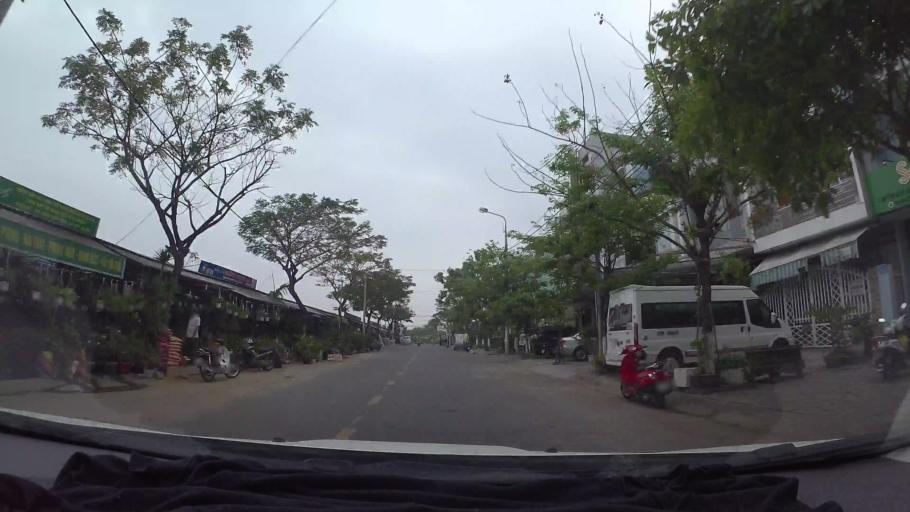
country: VN
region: Da Nang
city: Thanh Khe
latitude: 16.0552
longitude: 108.1850
